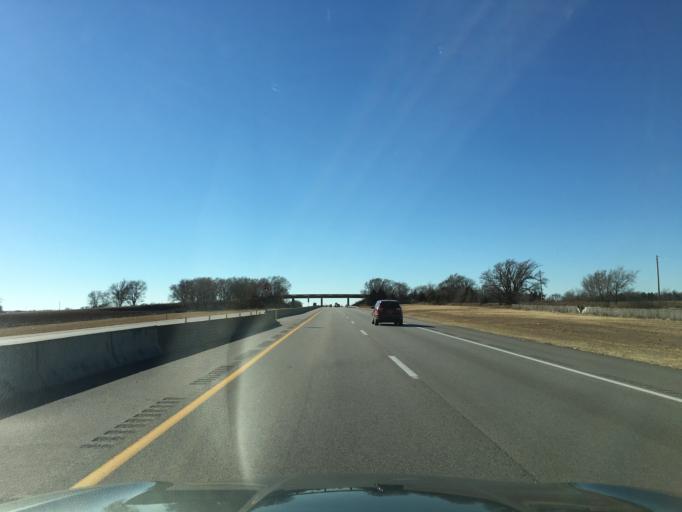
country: US
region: Kansas
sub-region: Sumner County
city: Belle Plaine
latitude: 37.3362
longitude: -97.3295
